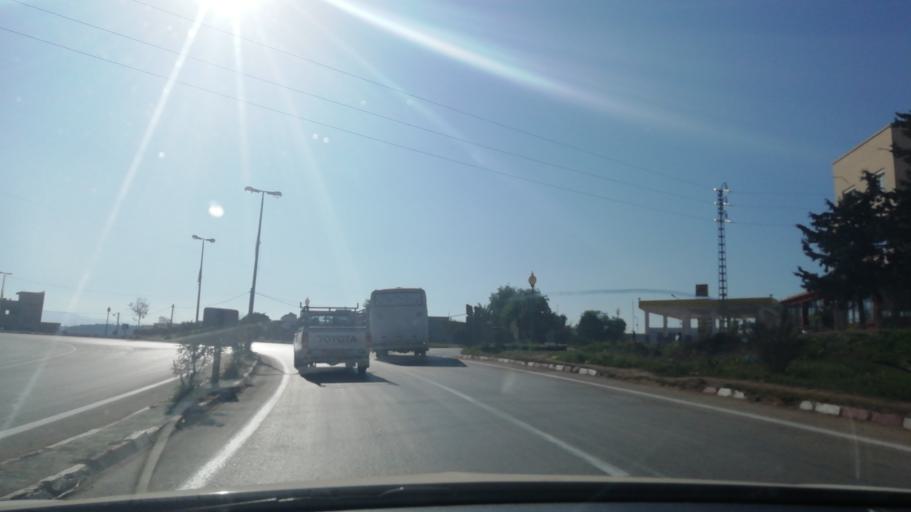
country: DZ
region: Tlemcen
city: Nedroma
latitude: 35.0934
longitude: -1.8344
